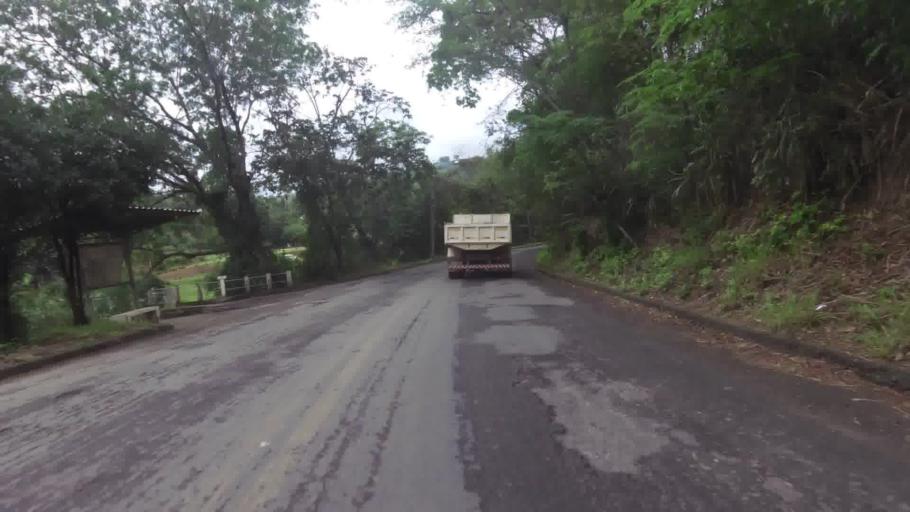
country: BR
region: Espirito Santo
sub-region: Iconha
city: Iconha
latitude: -20.7783
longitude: -40.8285
